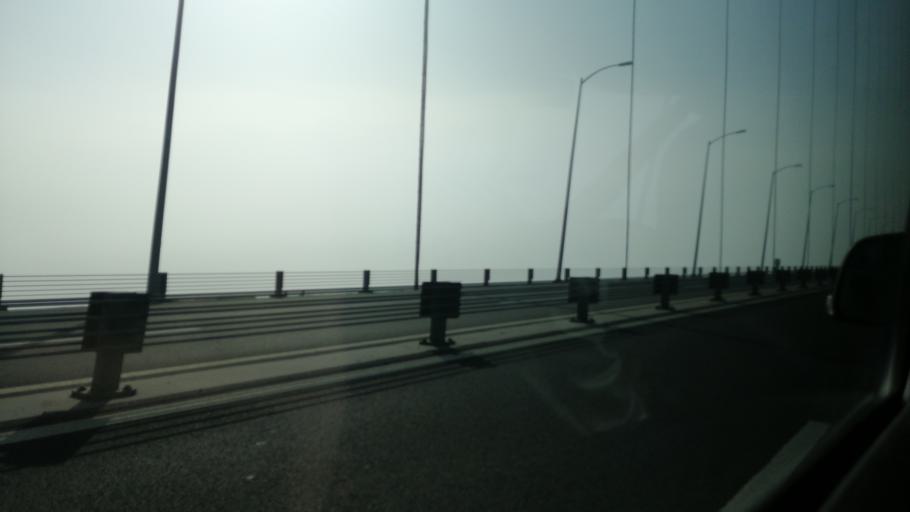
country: TR
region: Kocaeli
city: Tavsanli
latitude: 40.7658
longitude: 29.5174
